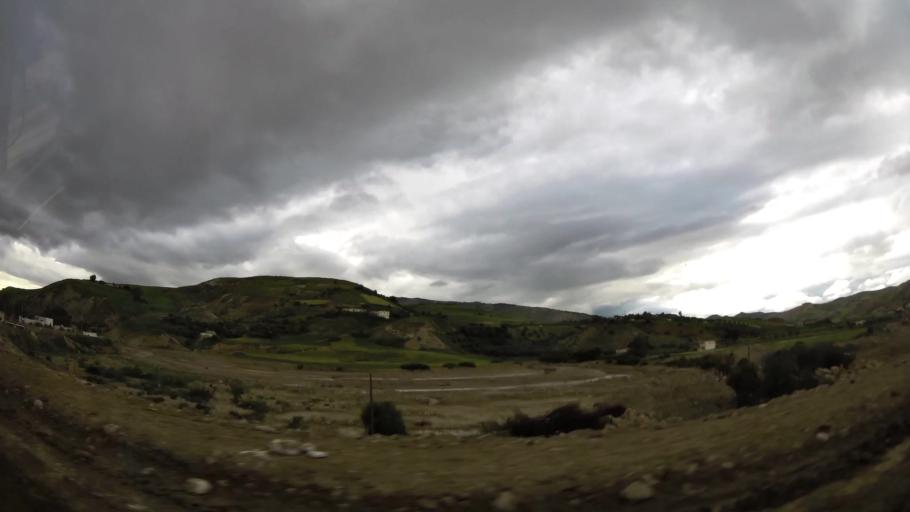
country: MA
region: Taza-Al Hoceima-Taounate
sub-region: Taza
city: Taza
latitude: 34.3478
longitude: -3.9218
